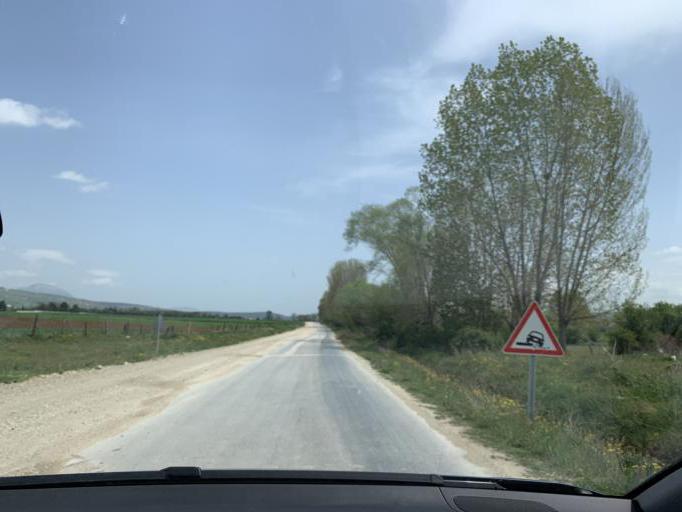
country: TR
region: Bolu
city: Bolu
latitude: 40.7446
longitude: 31.6574
